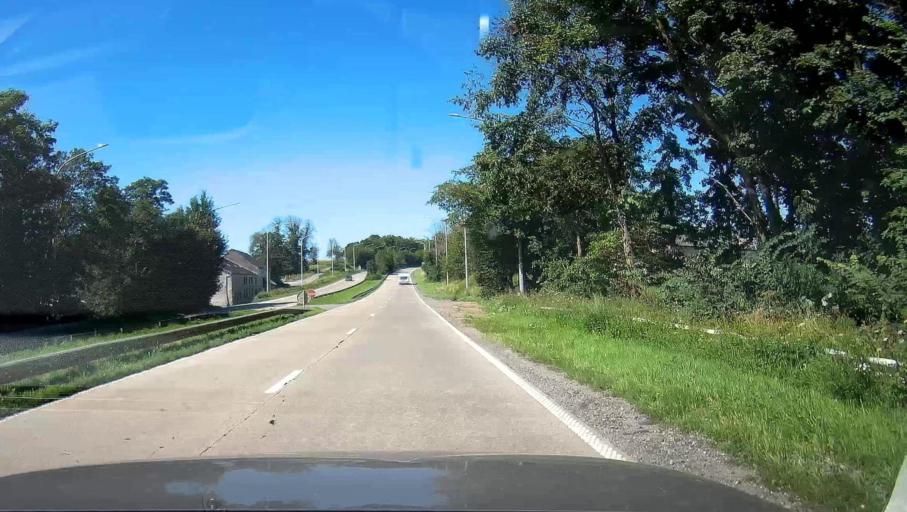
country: BE
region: Wallonia
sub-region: Province de Namur
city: Philippeville
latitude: 50.2227
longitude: 4.5120
